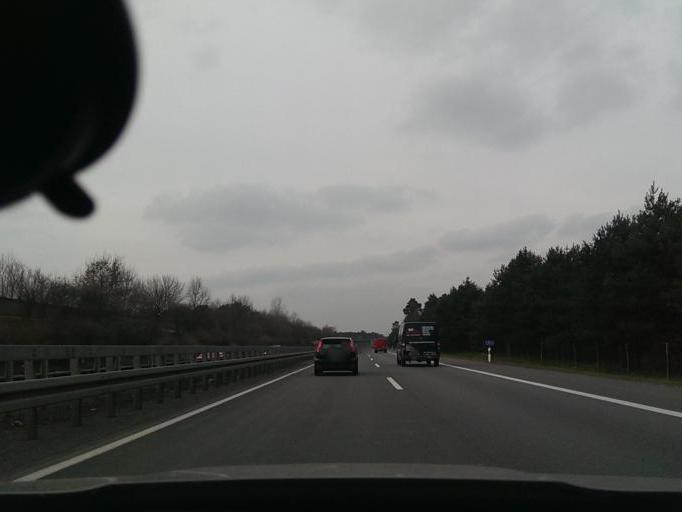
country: DE
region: North Rhine-Westphalia
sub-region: Regierungsbezirk Detmold
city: Hovelhof
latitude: 51.8733
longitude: 8.6523
